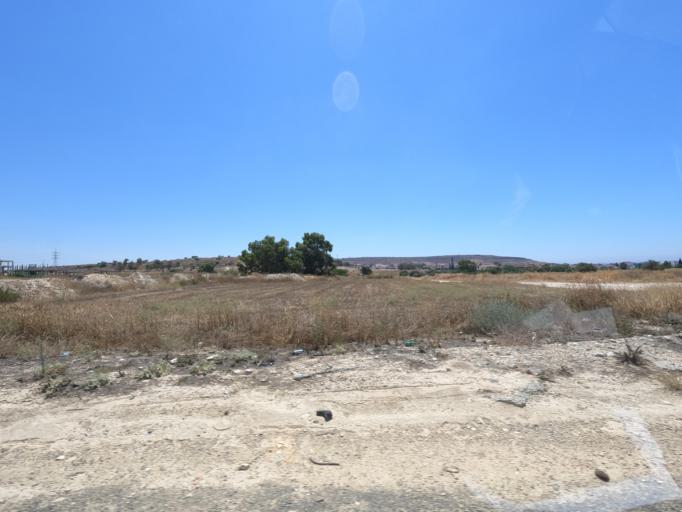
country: CY
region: Larnaka
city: Pyla
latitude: 35.0000
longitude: 33.6876
